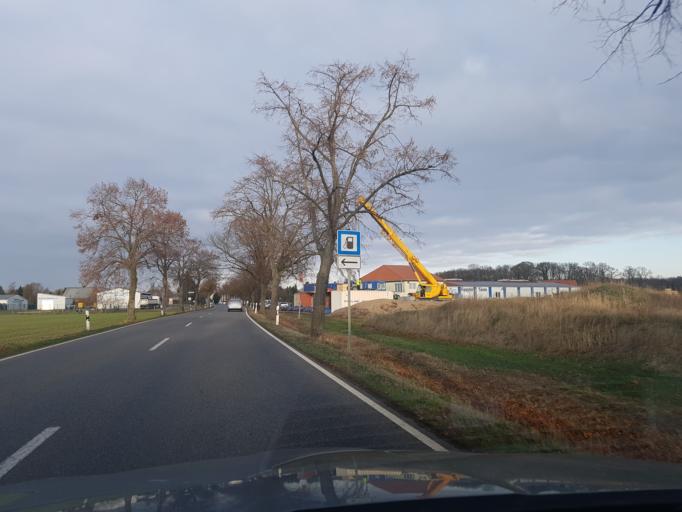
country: DE
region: Brandenburg
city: Kasel-Golzig
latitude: 51.9458
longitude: 13.6486
